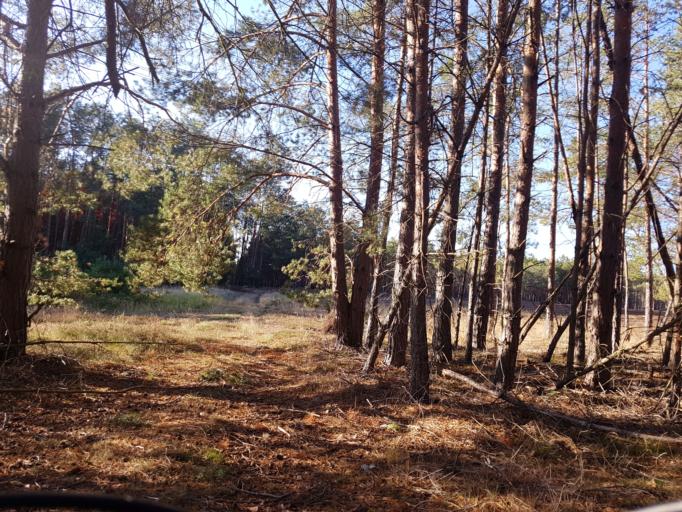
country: DE
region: Brandenburg
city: Schilda
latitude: 51.6212
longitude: 13.3693
